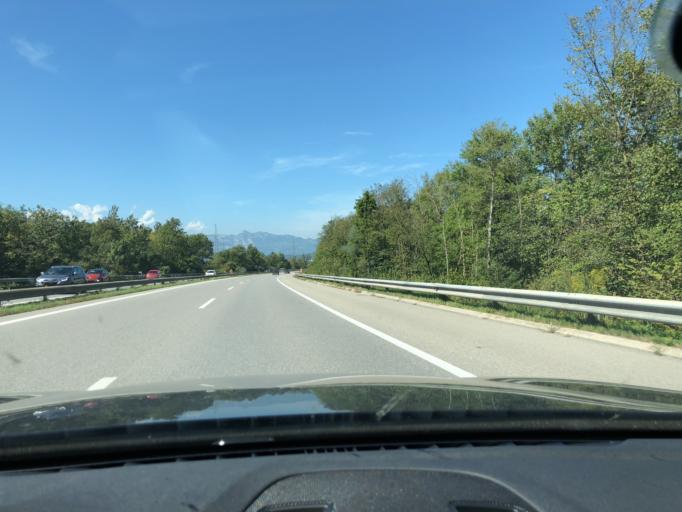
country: AT
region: Vorarlberg
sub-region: Politischer Bezirk Bludenz
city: Bludesch
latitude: 47.1783
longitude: 9.7330
